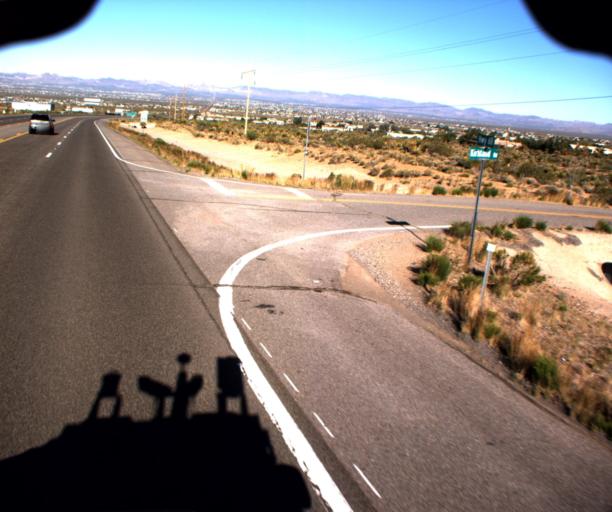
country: US
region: Arizona
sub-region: Mohave County
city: Golden Valley
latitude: 35.2188
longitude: -114.1383
